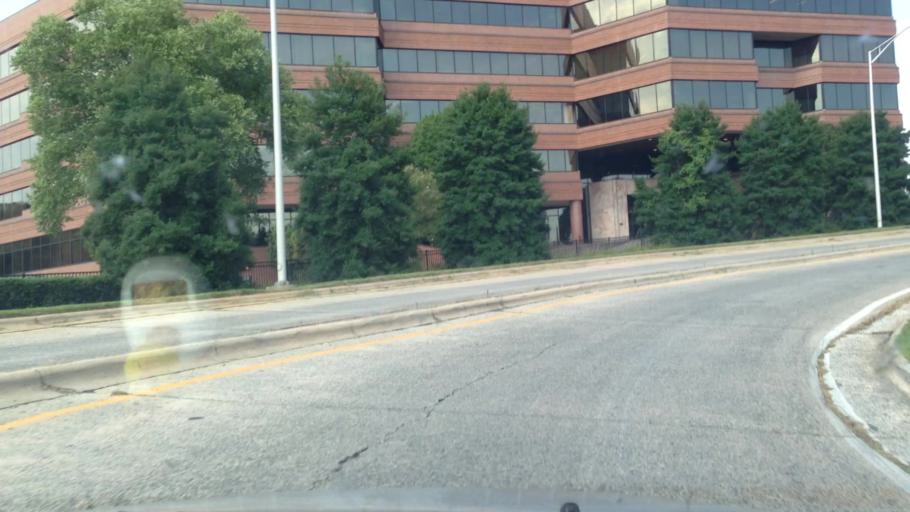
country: US
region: North Carolina
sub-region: Forsyth County
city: Winston-Salem
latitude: 36.0947
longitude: -80.2798
